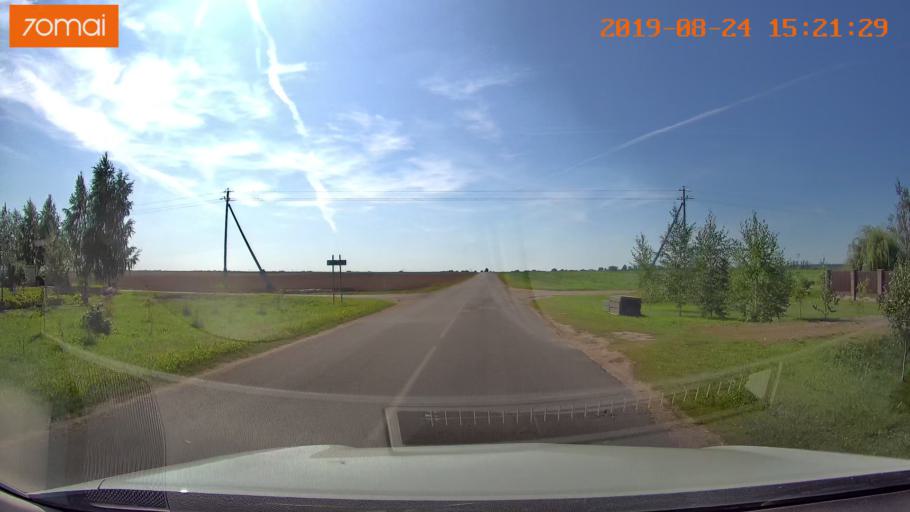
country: BY
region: Minsk
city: Samakhvalavichy
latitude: 53.6783
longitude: 27.5186
